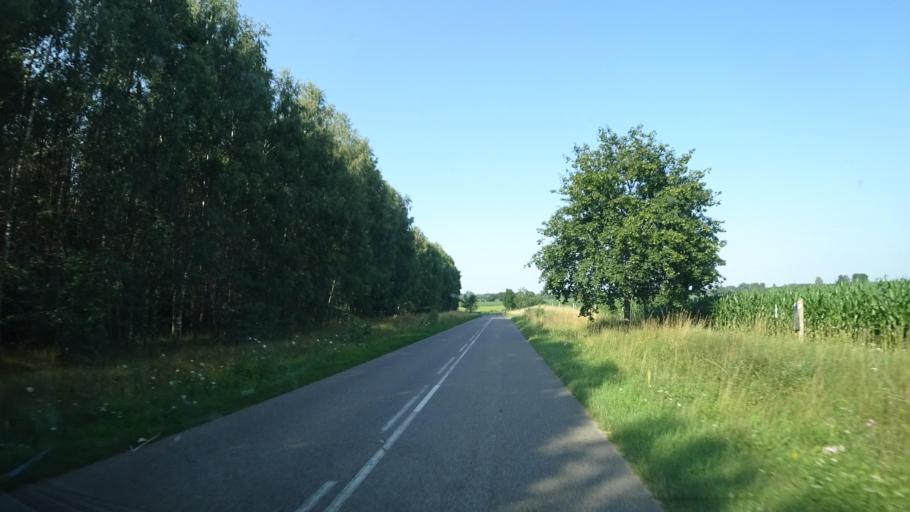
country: PL
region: Pomeranian Voivodeship
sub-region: Powiat czluchowski
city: Rzeczenica
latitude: 53.7781
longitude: 17.1600
